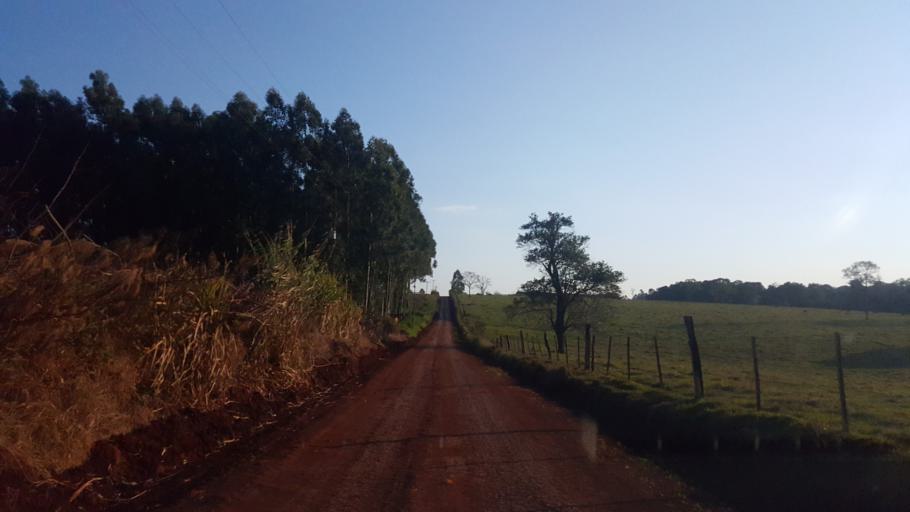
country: AR
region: Misiones
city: Capiovi
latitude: -26.9110
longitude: -55.0510
